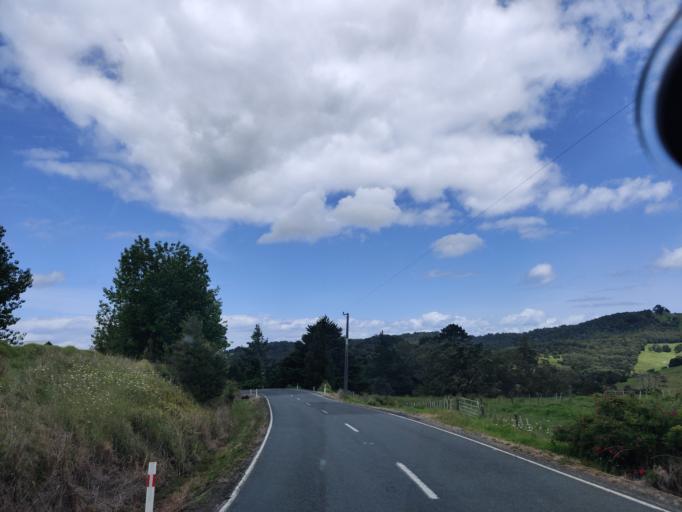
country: NZ
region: Northland
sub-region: Far North District
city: Kaitaia
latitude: -35.2867
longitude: 173.4866
